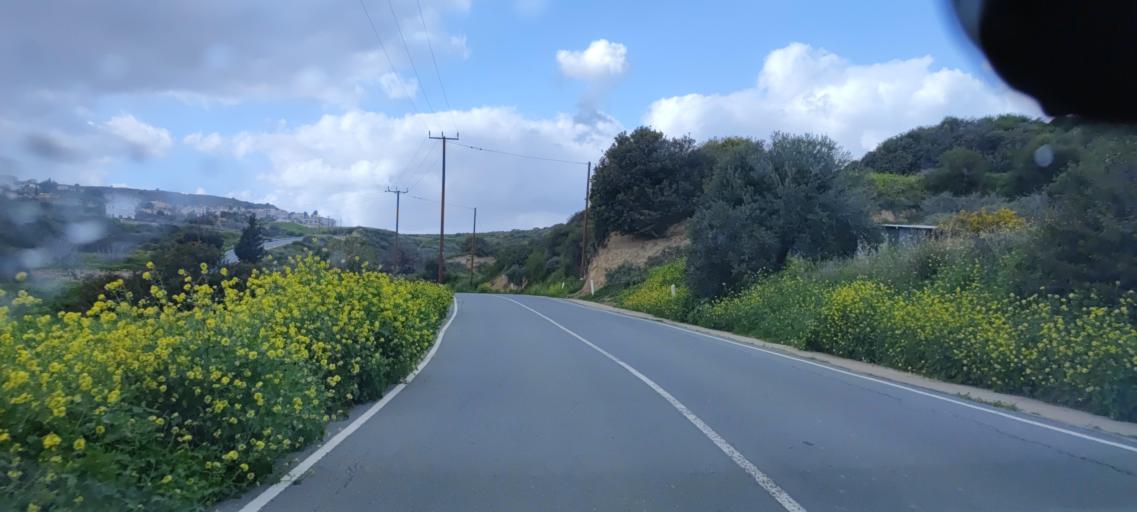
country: CY
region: Limassol
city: Pissouri
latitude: 34.6641
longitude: 32.7140
